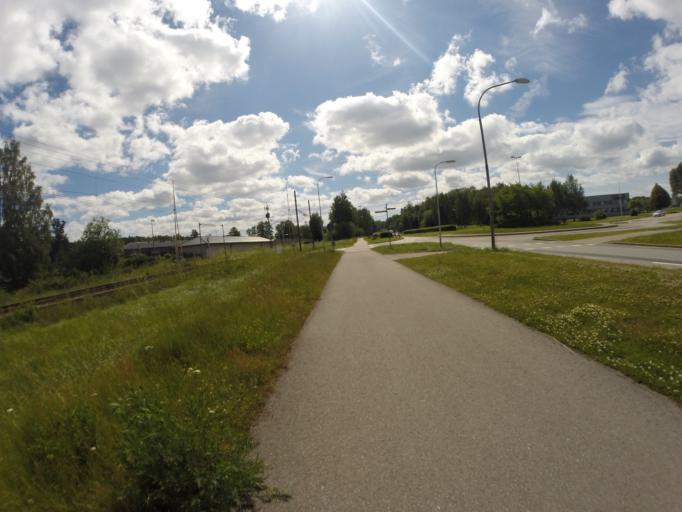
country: SE
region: Soedermanland
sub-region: Eskilstuna Kommun
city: Skogstorp
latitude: 59.3416
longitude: 16.4876
